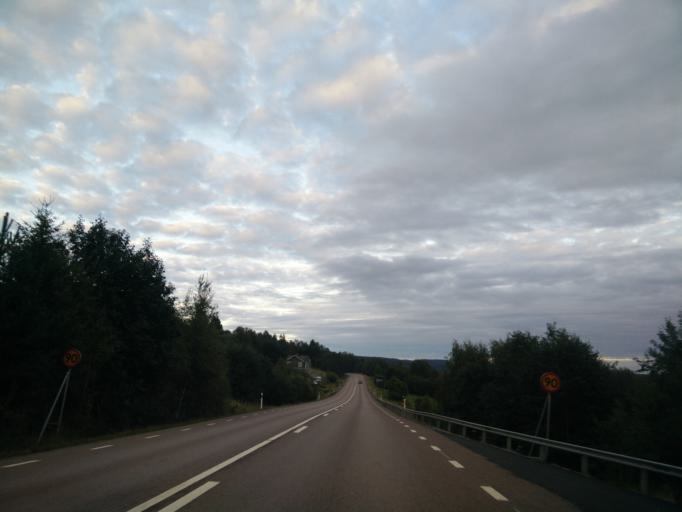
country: SE
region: Vaesternorrland
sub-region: Kramfors Kommun
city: Nordingra
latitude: 62.9204
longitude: 18.0535
